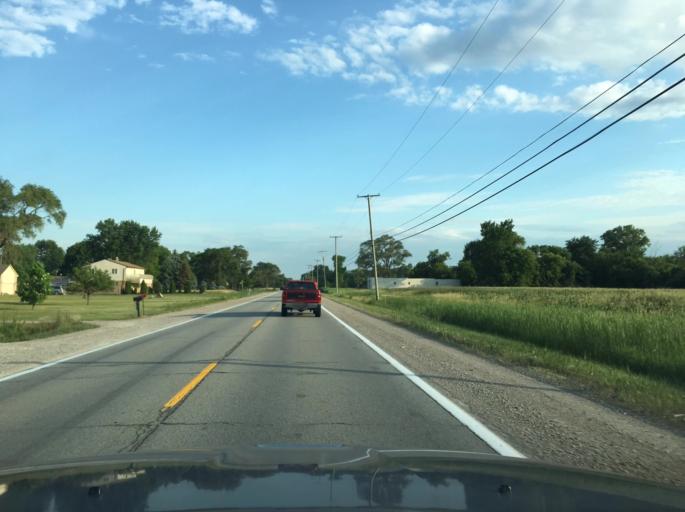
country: US
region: Michigan
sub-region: Macomb County
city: New Haven
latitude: 42.6981
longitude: -82.8788
